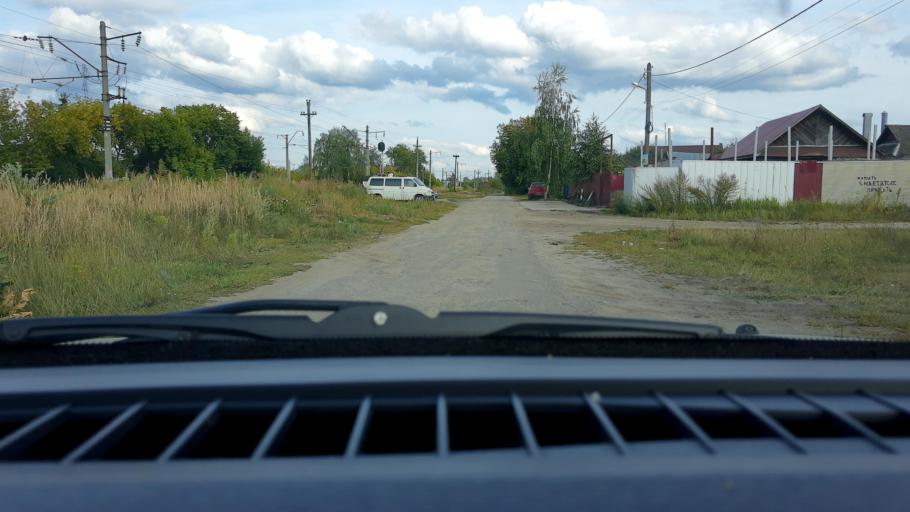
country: RU
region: Nizjnij Novgorod
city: Gorbatovka
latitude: 56.3727
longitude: 43.8146
